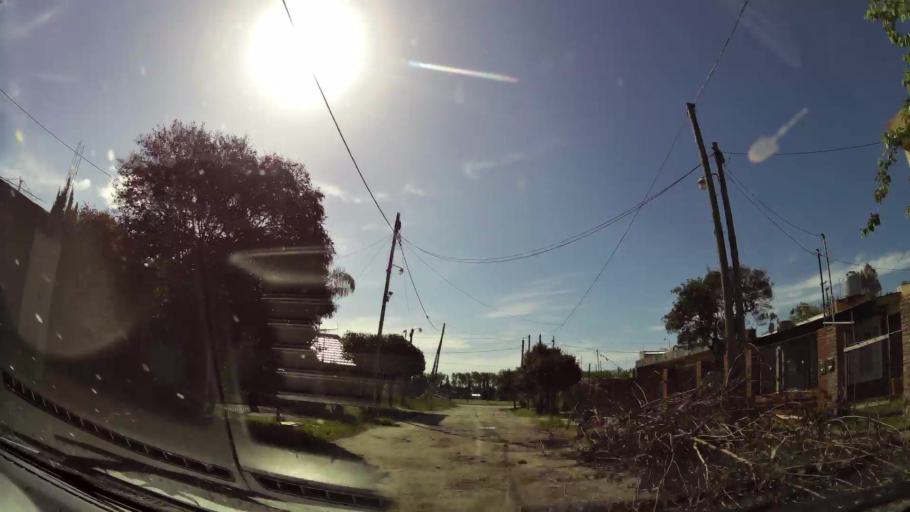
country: AR
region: Buenos Aires
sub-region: Partido de Quilmes
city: Quilmes
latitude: -34.8080
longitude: -58.2260
